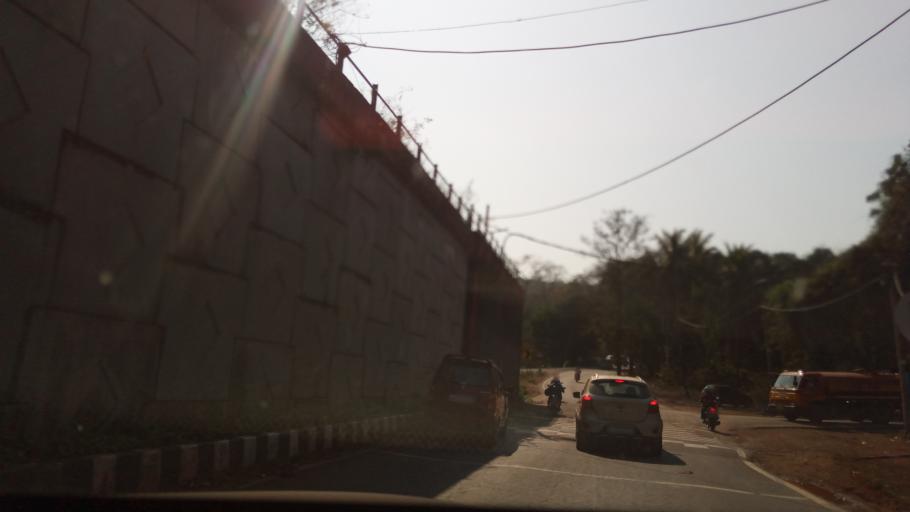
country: IN
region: Goa
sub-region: North Goa
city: Curti
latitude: 15.4245
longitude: 74.0458
